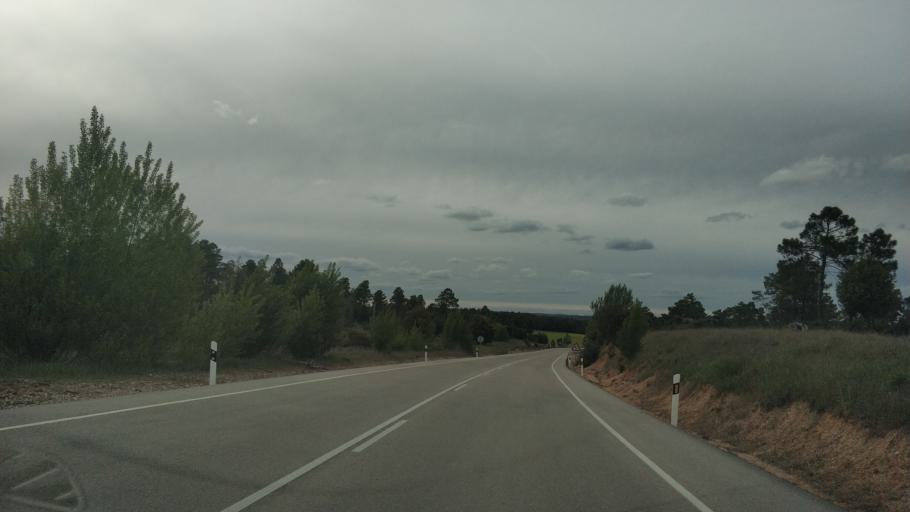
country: ES
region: Castille and Leon
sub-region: Provincia de Soria
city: Valdenebro
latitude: 41.5449
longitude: -2.9582
